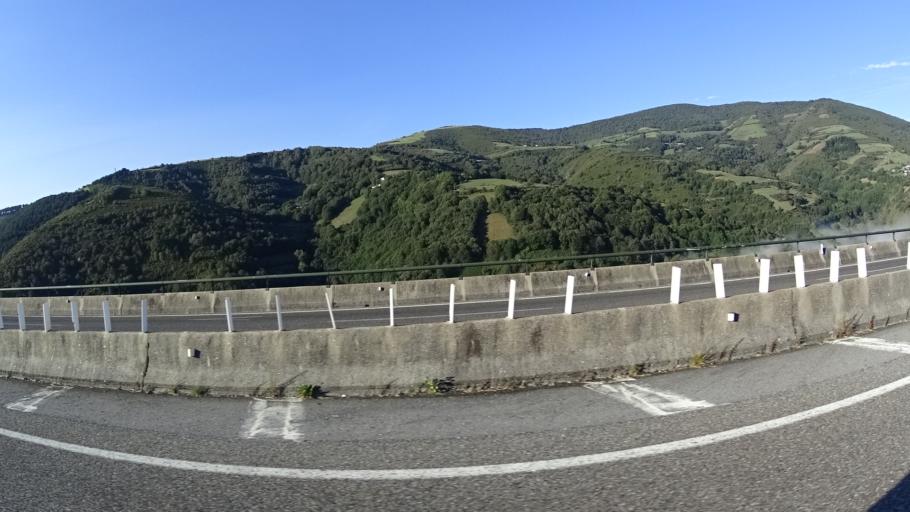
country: ES
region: Galicia
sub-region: Provincia de Lugo
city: San Roman
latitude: 42.7529
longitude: -7.0666
